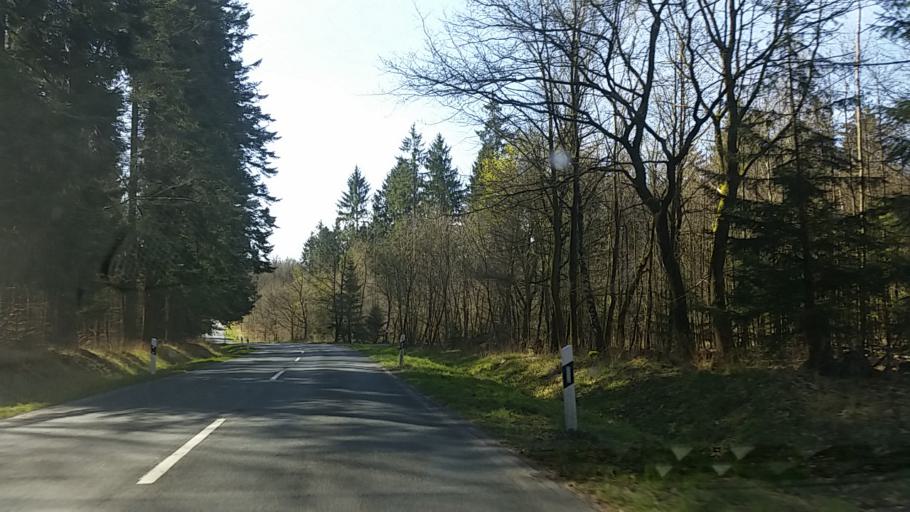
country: DE
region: Lower Saxony
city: Rabke
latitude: 52.1709
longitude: 10.8571
